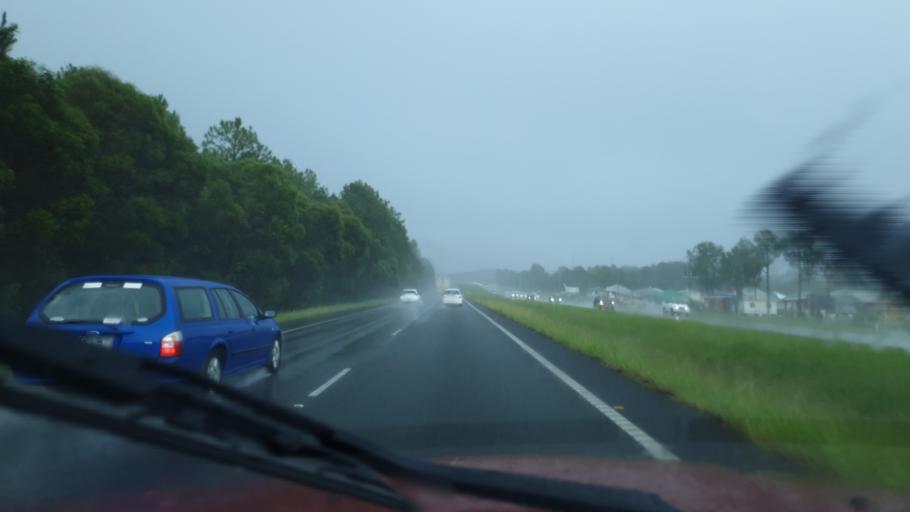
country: AU
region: Queensland
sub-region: Moreton Bay
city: Caboolture
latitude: -27.0503
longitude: 152.9770
